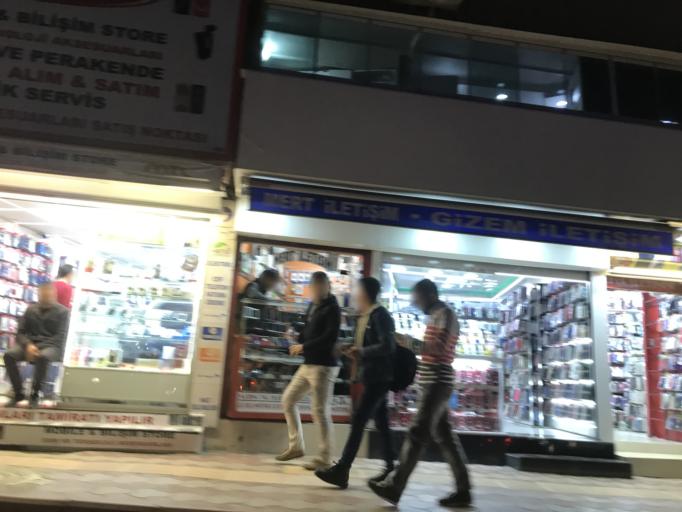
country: TR
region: Hatay
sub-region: Antakya Ilcesi
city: Antakya
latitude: 36.2034
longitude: 36.1618
